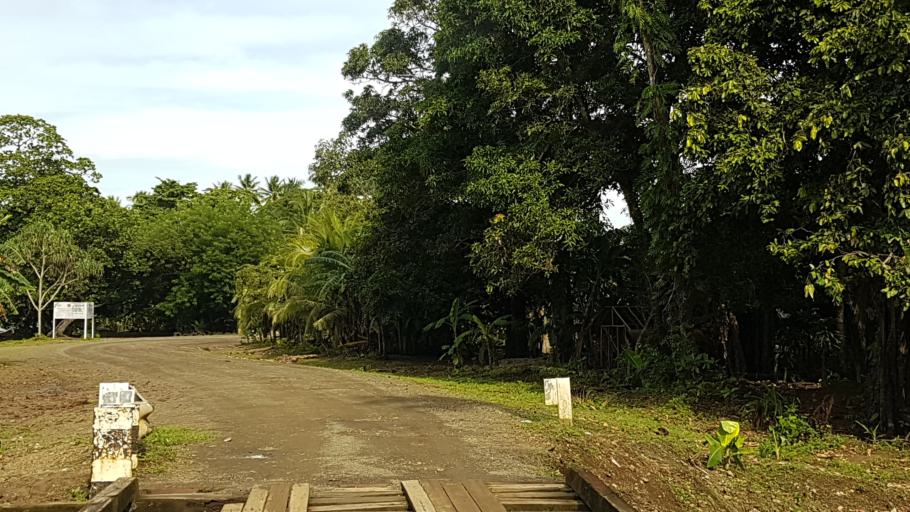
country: PG
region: Milne Bay
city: Alotau
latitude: -10.3236
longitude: 150.6830
